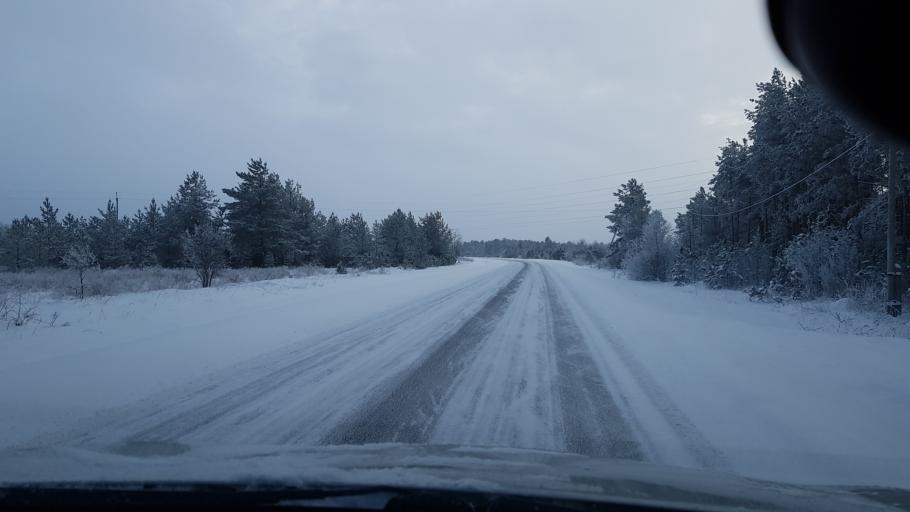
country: EE
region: Harju
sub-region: Keila linn
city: Keila
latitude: 59.3517
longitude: 24.4274
